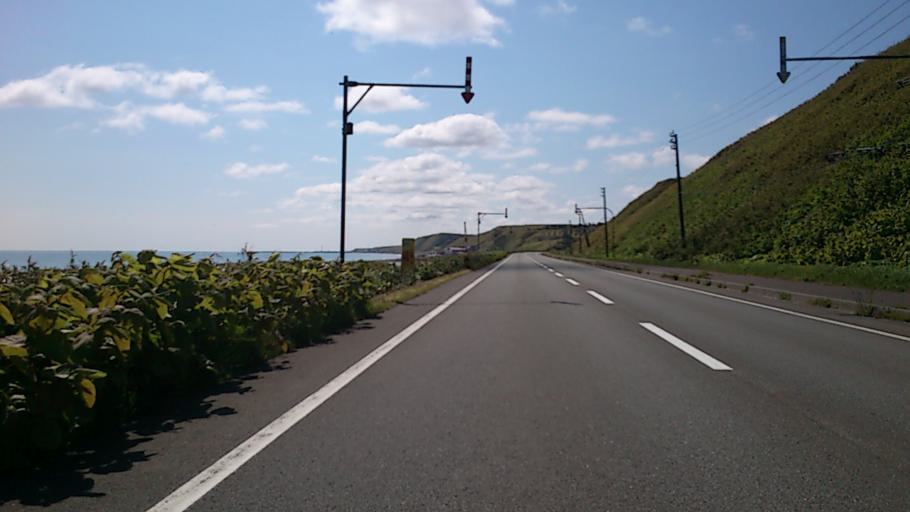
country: JP
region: Hokkaido
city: Makubetsu
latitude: 45.4038
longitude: 142.0462
